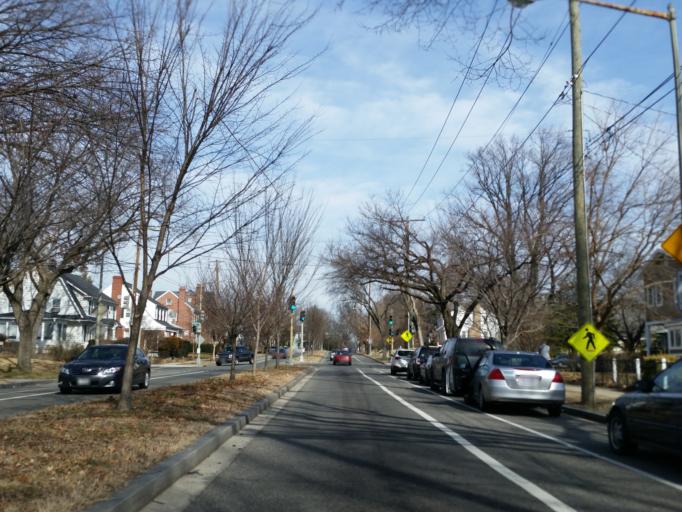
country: US
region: Maryland
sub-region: Montgomery County
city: Takoma Park
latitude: 38.9718
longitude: -77.0240
